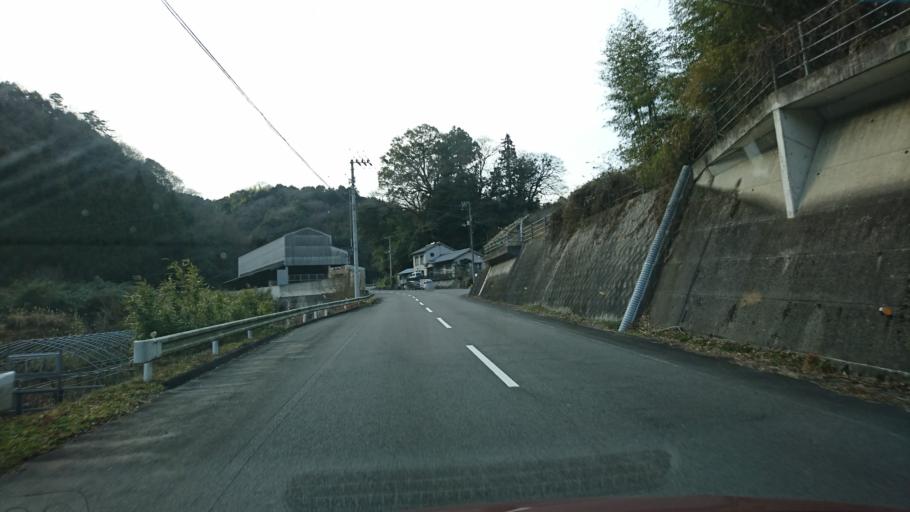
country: JP
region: Ehime
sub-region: Shikoku-chuo Shi
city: Matsuyama
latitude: 33.8993
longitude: 132.8283
